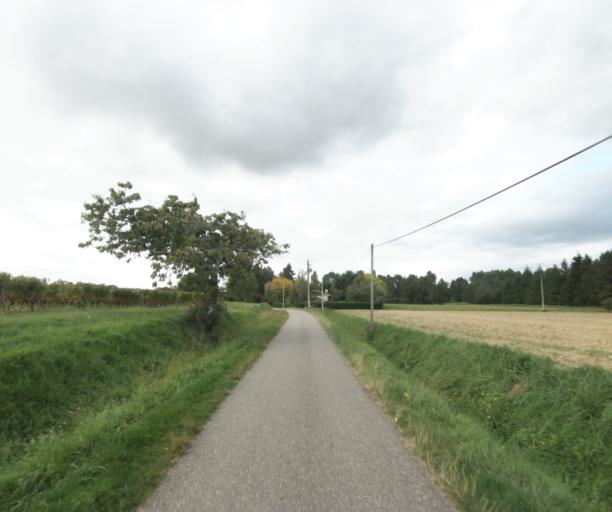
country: FR
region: Midi-Pyrenees
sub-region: Departement du Gers
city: Eauze
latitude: 43.9288
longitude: 0.0828
